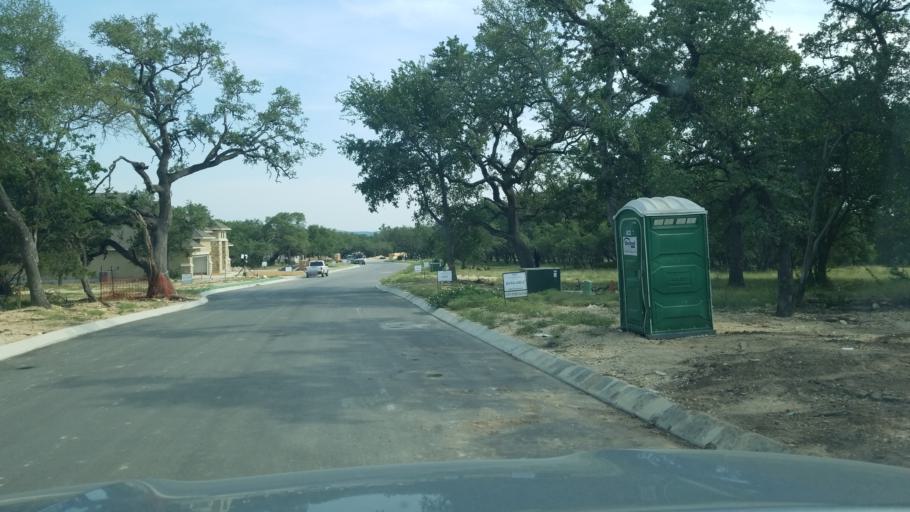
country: US
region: Texas
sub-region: Bexar County
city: Scenic Oaks
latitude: 29.7286
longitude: -98.6617
